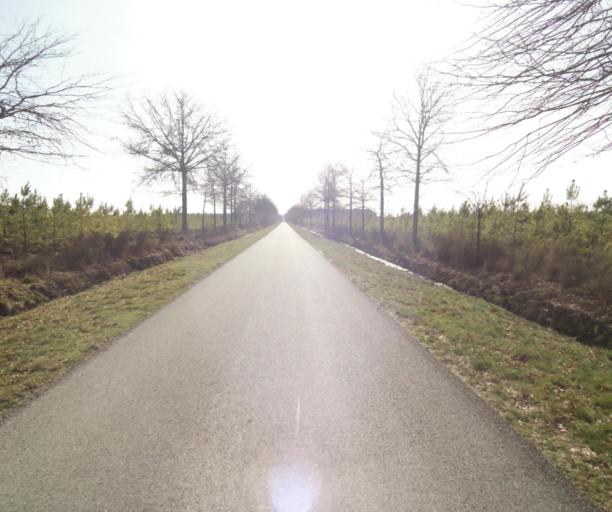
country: FR
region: Aquitaine
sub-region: Departement des Landes
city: Roquefort
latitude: 44.1685
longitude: -0.1634
